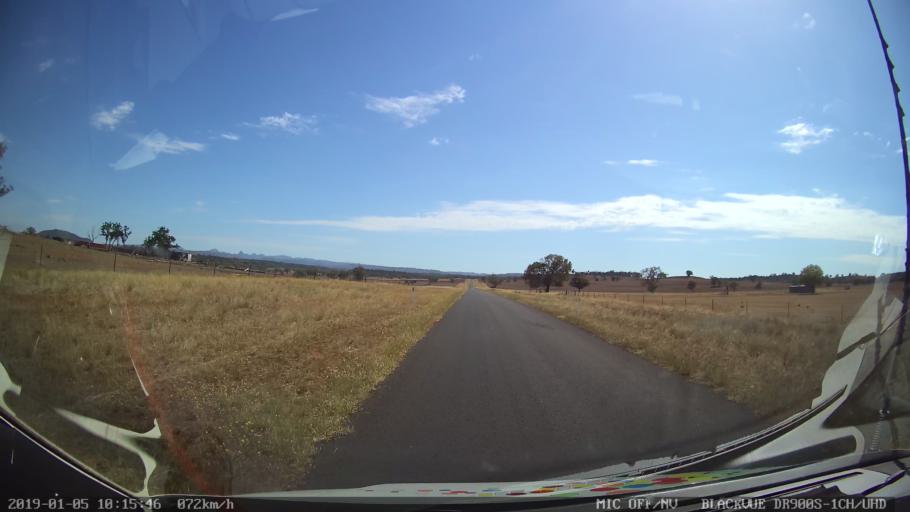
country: AU
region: New South Wales
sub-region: Gilgandra
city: Gilgandra
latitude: -31.5811
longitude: 148.9460
